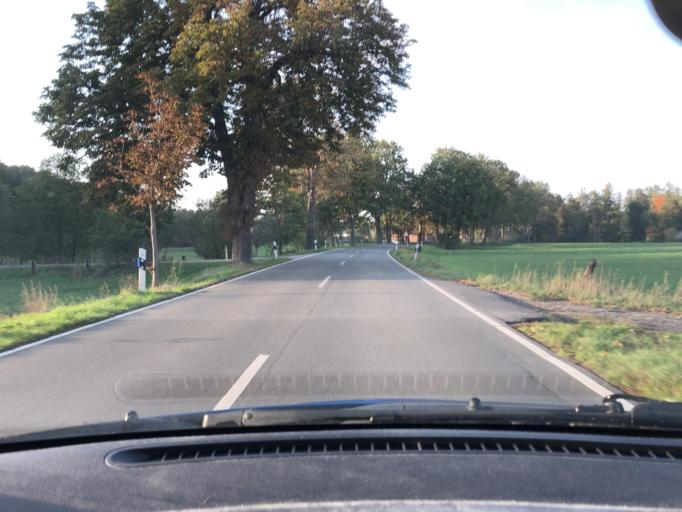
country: DE
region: Lower Saxony
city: Hitzacker
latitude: 53.1156
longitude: 11.0547
